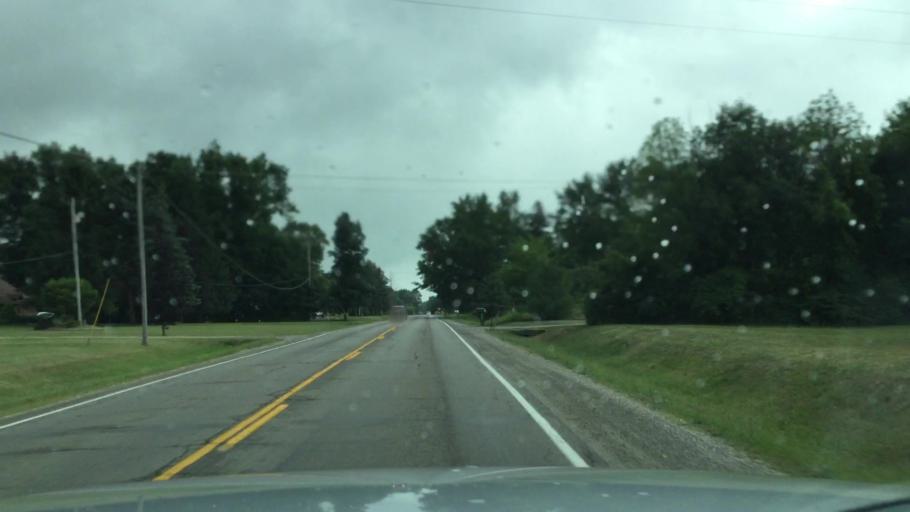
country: US
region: Michigan
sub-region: Genesee County
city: Clio
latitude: 43.1539
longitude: -83.7740
